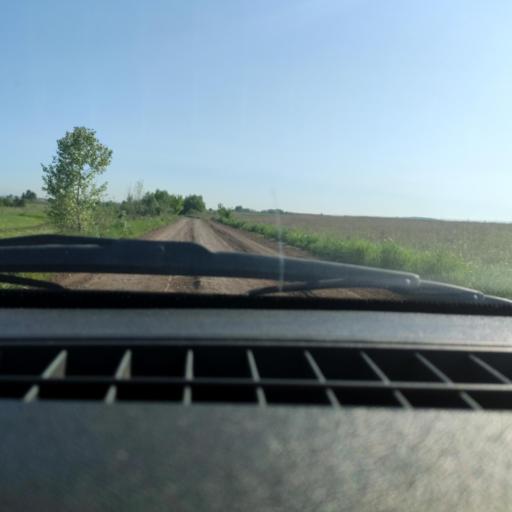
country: RU
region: Bashkortostan
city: Avdon
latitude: 54.5702
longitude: 55.8367
